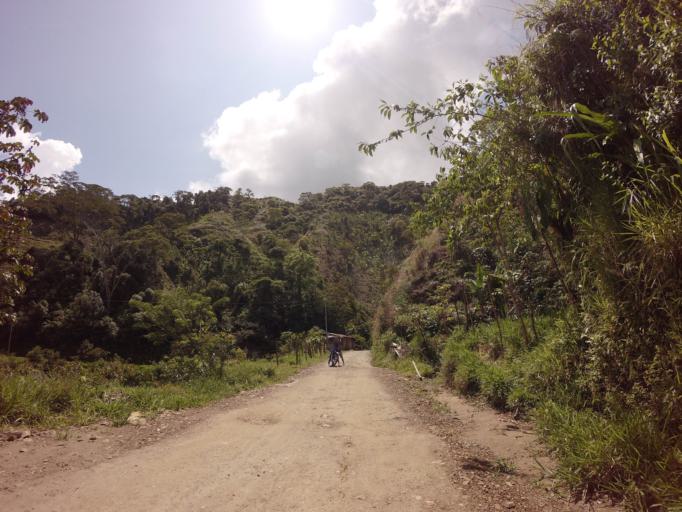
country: CO
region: Caldas
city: Pensilvania
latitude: 5.4926
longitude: -75.1871
